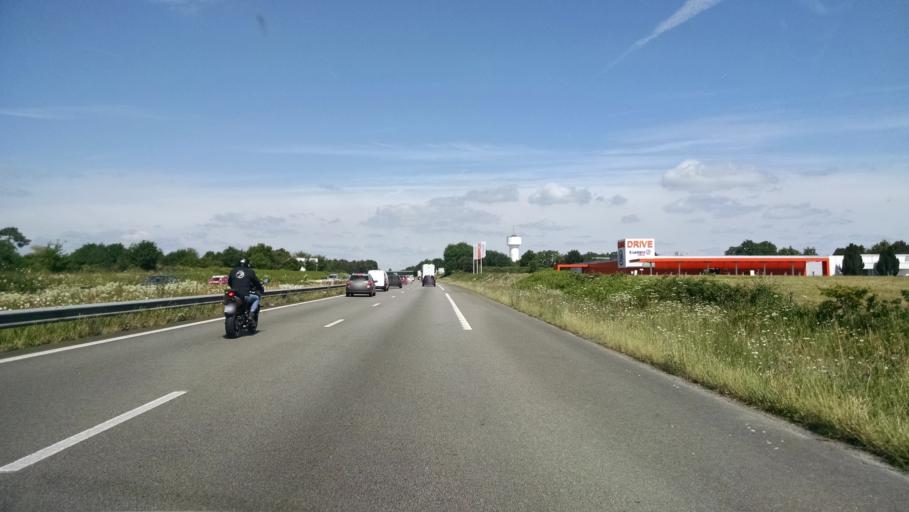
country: FR
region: Pays de la Loire
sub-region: Departement de la Loire-Atlantique
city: Sautron
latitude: 47.2754
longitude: -1.7204
